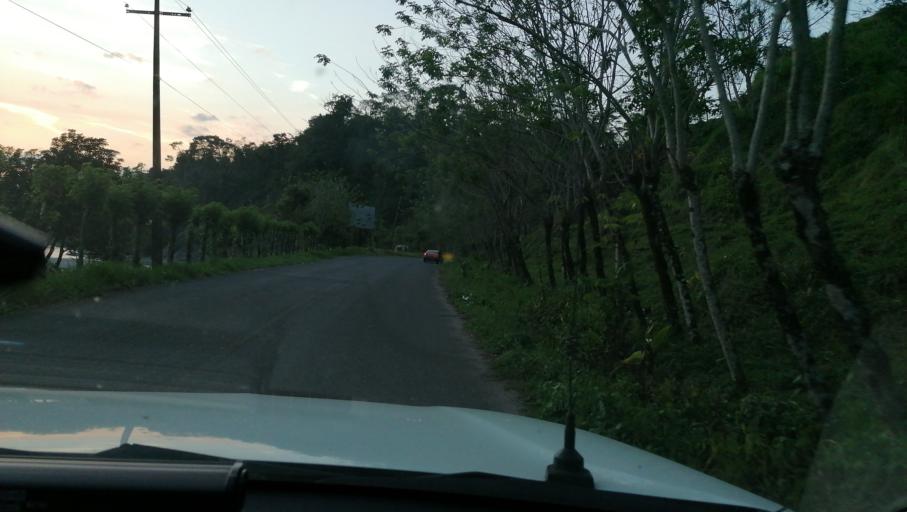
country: MX
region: Chiapas
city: Ostuacan
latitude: 17.4169
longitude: -93.3408
